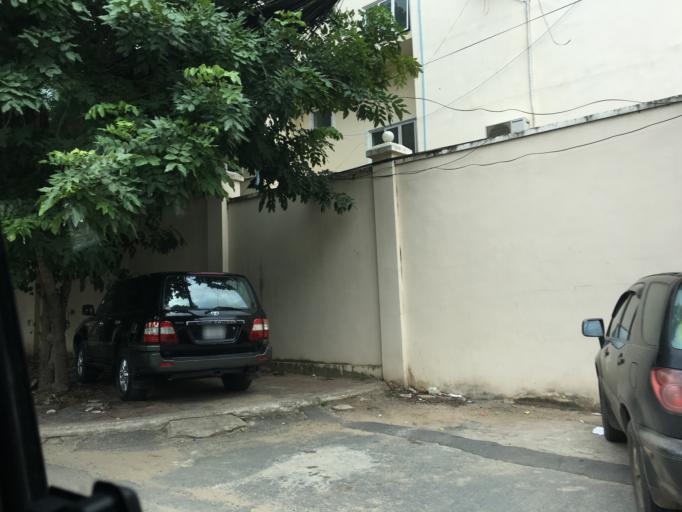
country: KH
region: Phnom Penh
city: Phnom Penh
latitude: 11.5384
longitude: 104.9271
